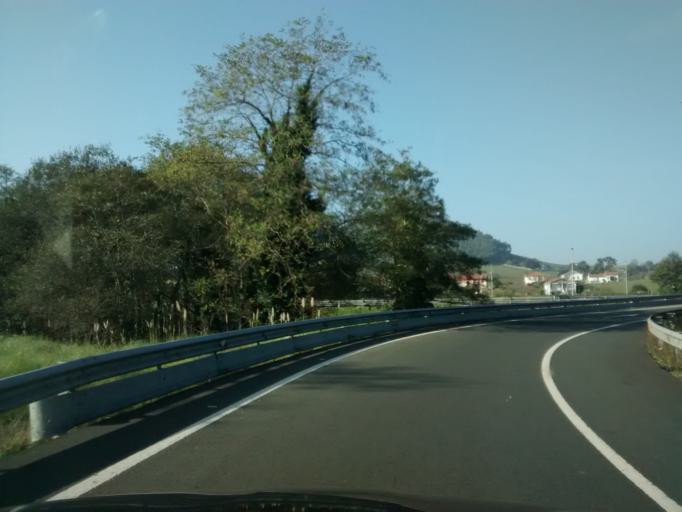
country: ES
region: Cantabria
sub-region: Provincia de Cantabria
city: Miengo
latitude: 43.4161
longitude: -3.9619
